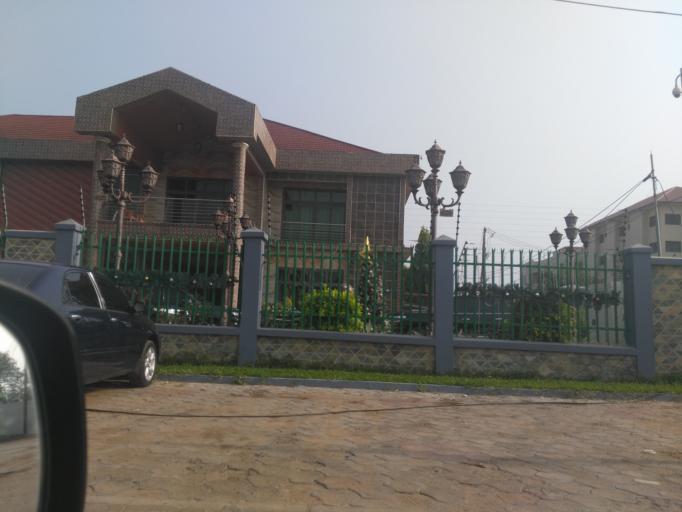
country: GH
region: Greater Accra
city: Accra
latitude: 5.6057
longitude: -0.2010
